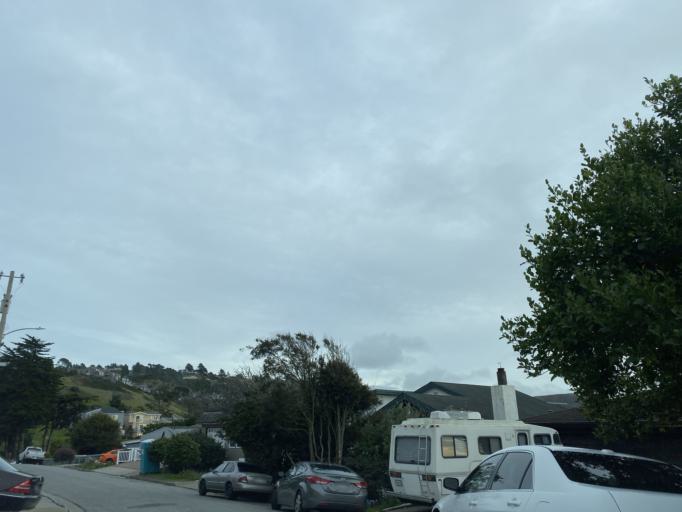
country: US
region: California
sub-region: San Mateo County
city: Broadmoor
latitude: 37.6555
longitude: -122.4859
